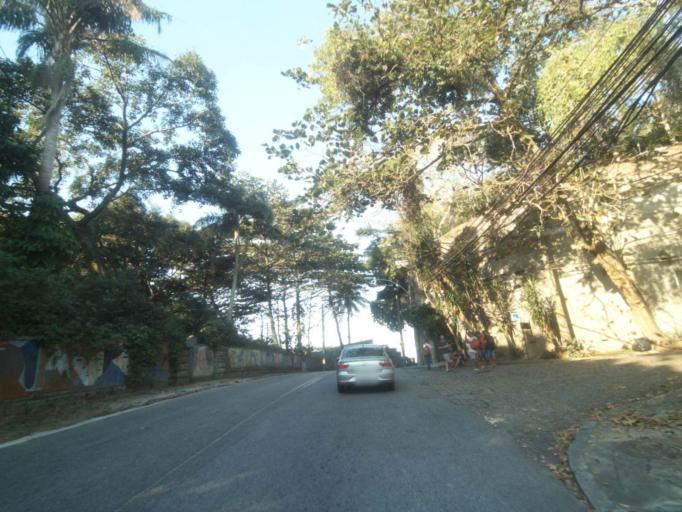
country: BR
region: Rio de Janeiro
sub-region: Rio De Janeiro
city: Rio de Janeiro
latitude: -23.0080
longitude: -43.2885
